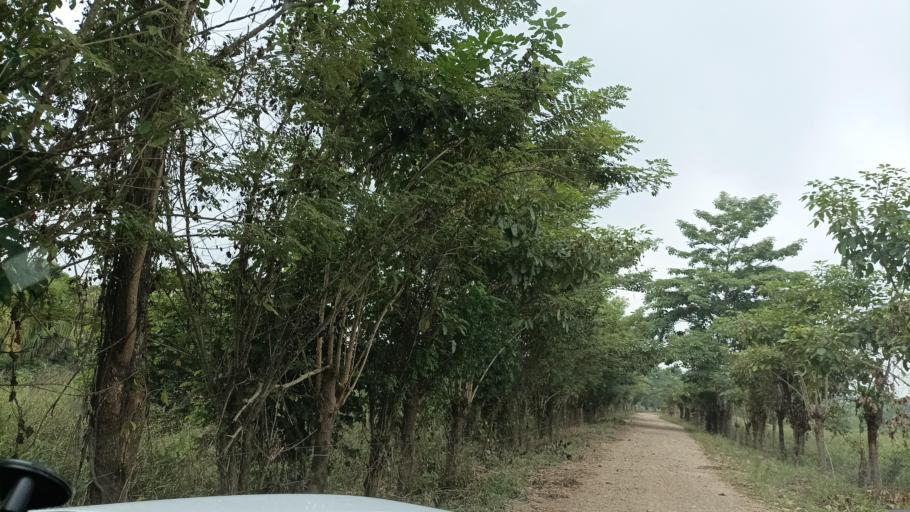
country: MX
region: Veracruz
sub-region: Uxpanapa
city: Poblado 10
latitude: 17.5668
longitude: -94.2261
